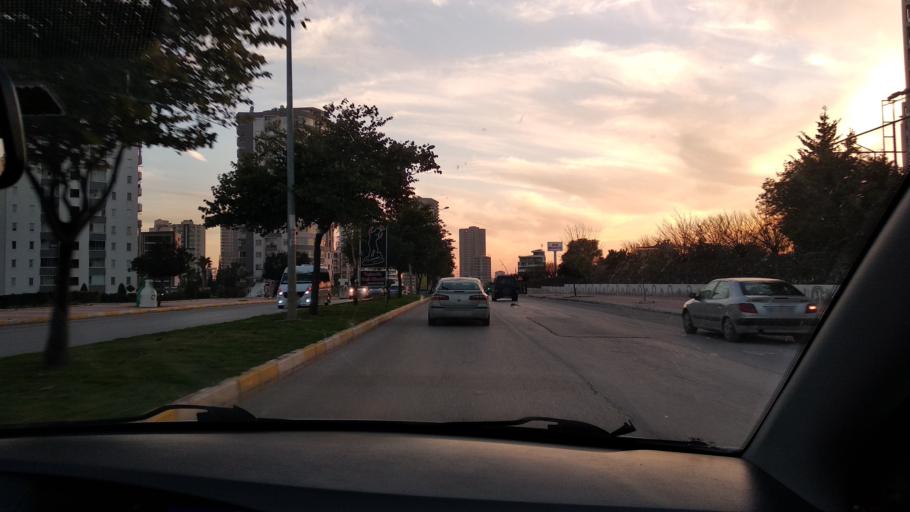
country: TR
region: Mersin
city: Mercin
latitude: 36.8051
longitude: 34.5863
